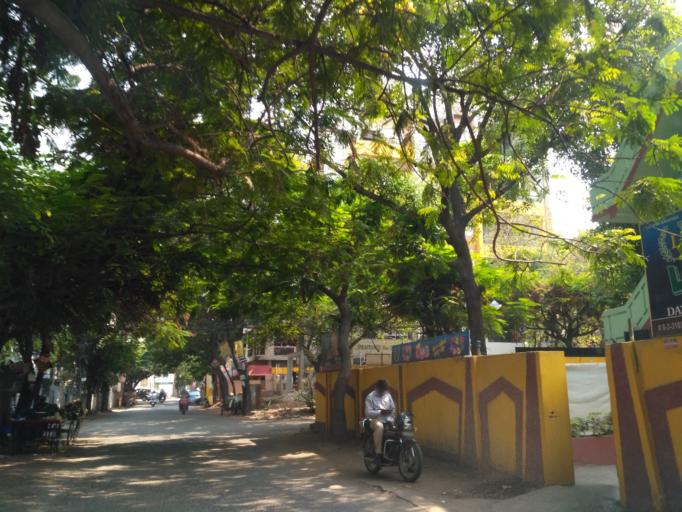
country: IN
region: Telangana
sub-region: Rangareddi
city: Kukatpalli
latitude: 17.4361
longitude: 78.4365
